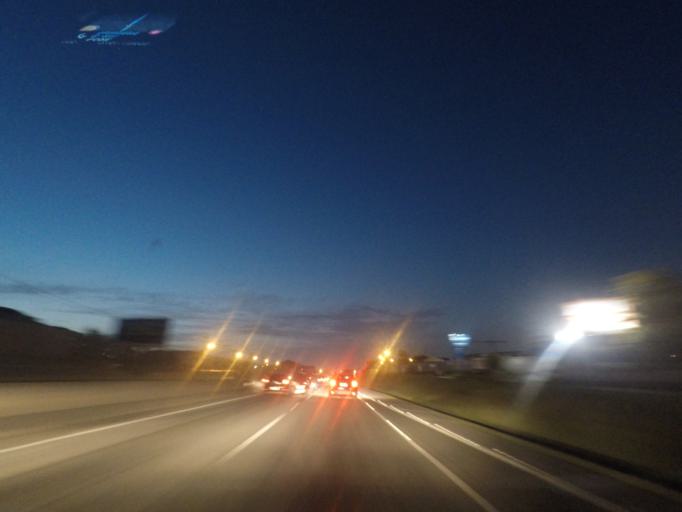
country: BR
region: Parana
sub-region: Pinhais
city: Pinhais
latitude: -25.4629
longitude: -49.2181
